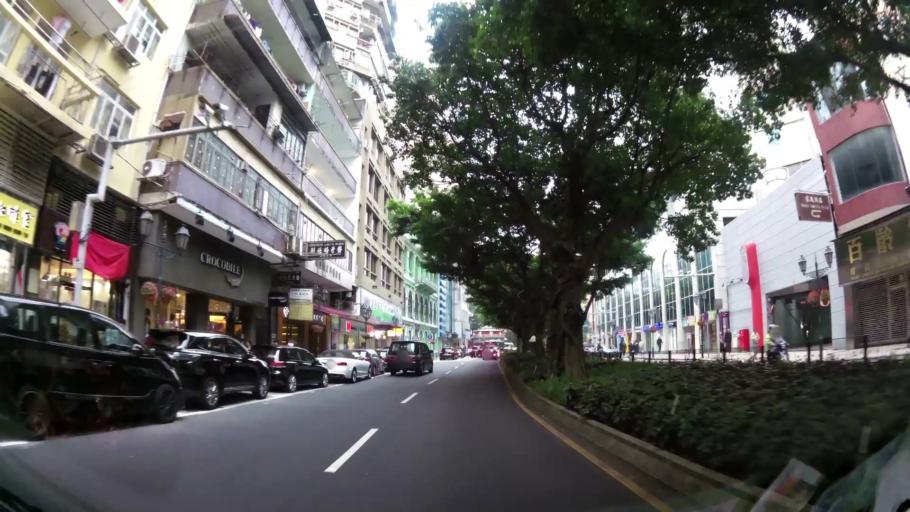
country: MO
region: Macau
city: Macau
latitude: 22.1928
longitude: 113.5422
